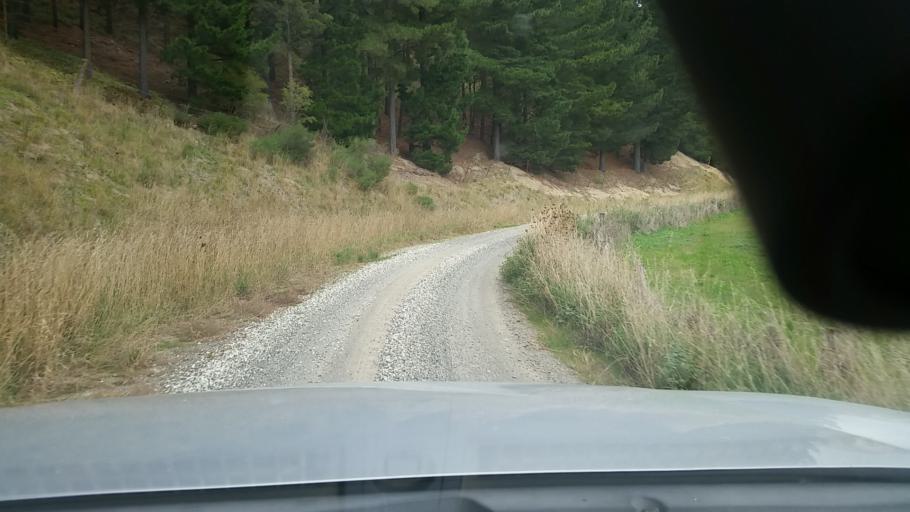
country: NZ
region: Marlborough
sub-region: Marlborough District
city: Blenheim
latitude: -41.6951
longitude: 174.1241
